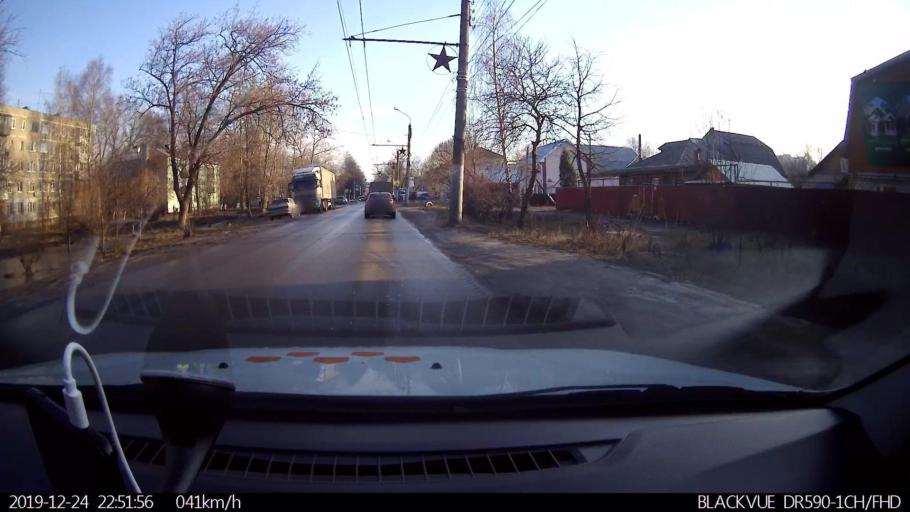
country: RU
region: Nizjnij Novgorod
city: Nizhniy Novgorod
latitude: 56.2869
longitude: 43.9155
